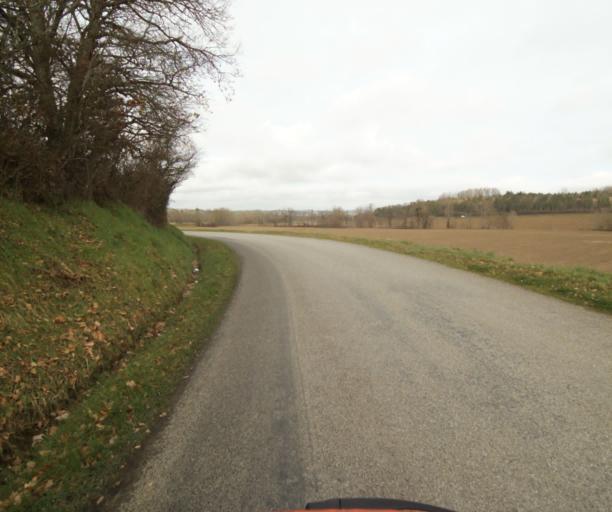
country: FR
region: Midi-Pyrenees
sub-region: Departement de l'Ariege
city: Pamiers
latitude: 43.1017
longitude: 1.5539
